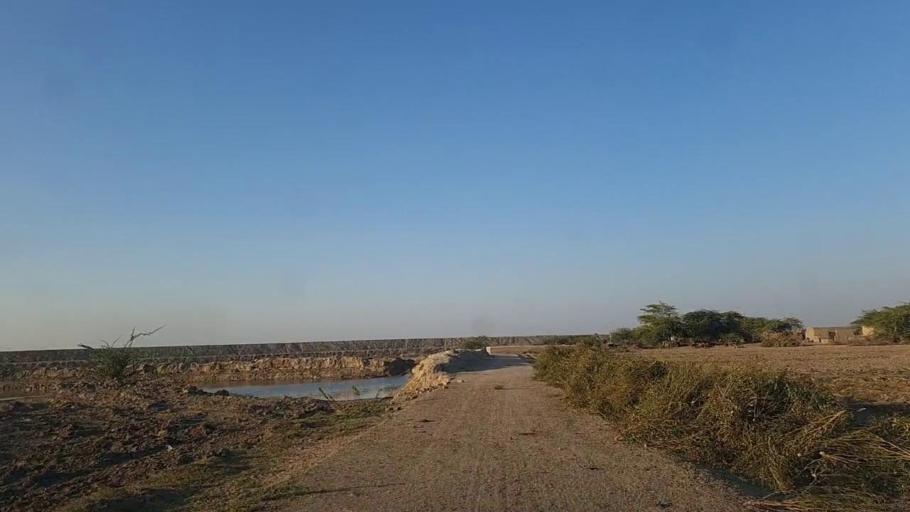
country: PK
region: Sindh
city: Naukot
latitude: 25.0072
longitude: 69.4266
